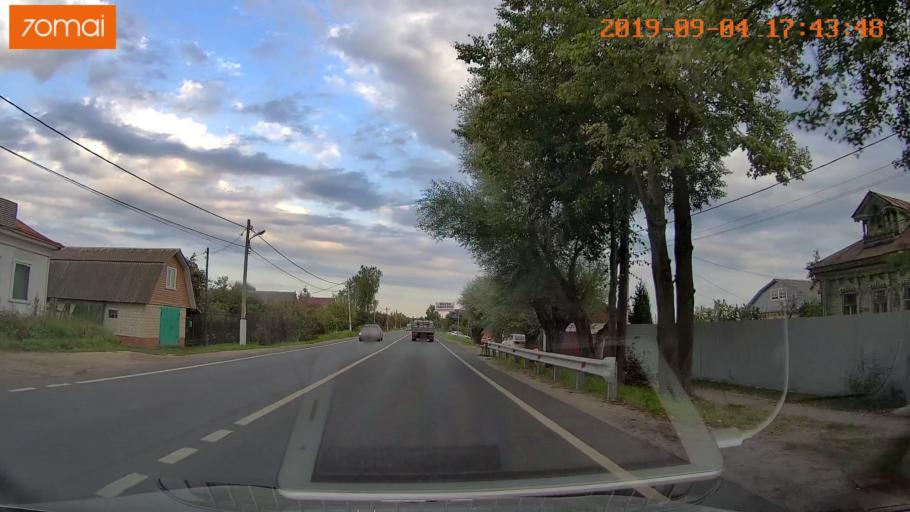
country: RU
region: Moskovskaya
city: Imeni Tsyurupy
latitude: 55.5759
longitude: 38.5911
